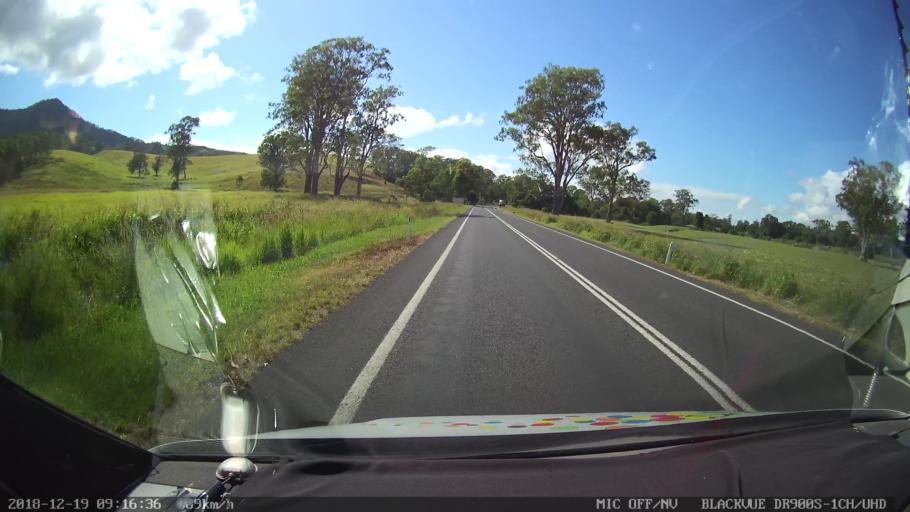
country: AU
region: New South Wales
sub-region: Kyogle
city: Kyogle
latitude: -28.5230
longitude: 152.9688
